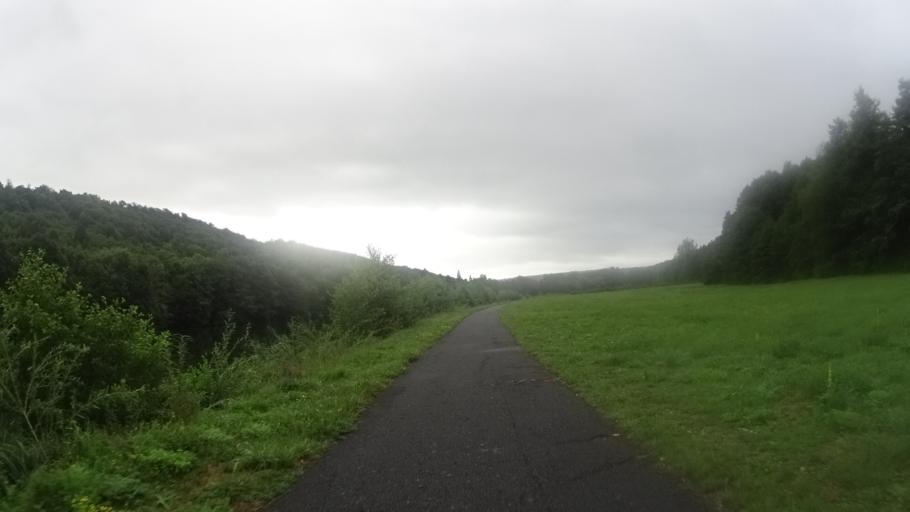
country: FR
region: Lorraine
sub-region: Departement de Meurthe-et-Moselle
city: Chaligny
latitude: 48.6483
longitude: 6.0396
